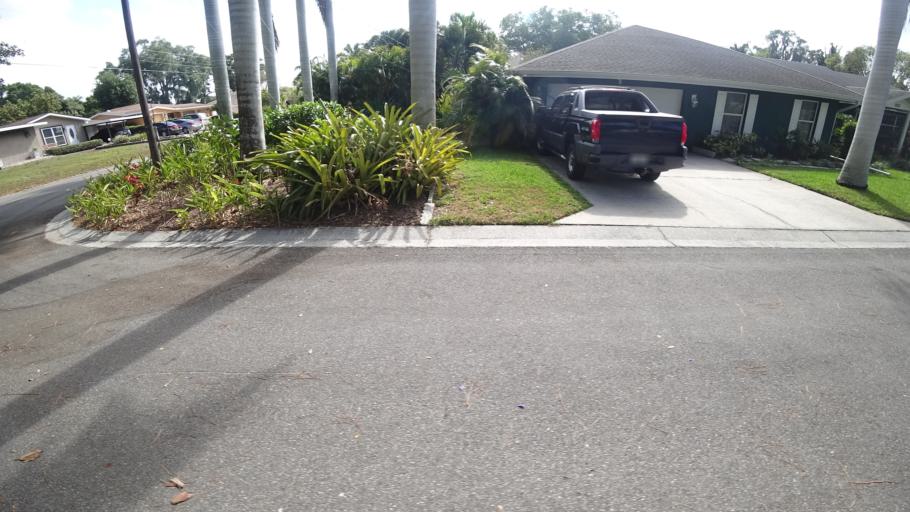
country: US
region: Florida
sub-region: Manatee County
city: Whitfield
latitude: 27.4192
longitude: -82.5673
